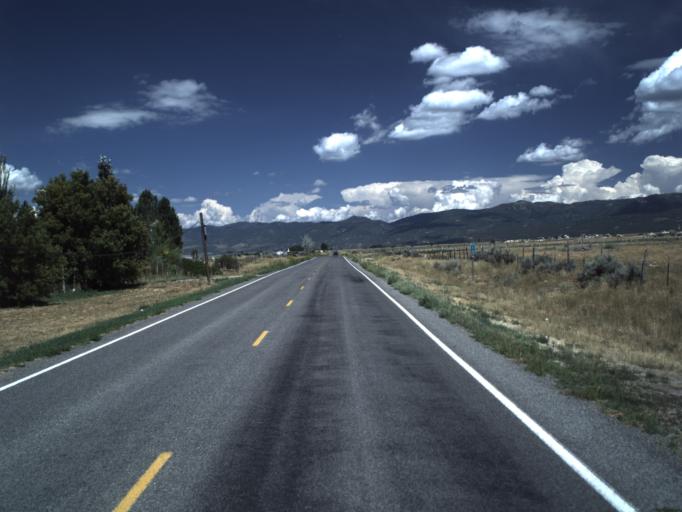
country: US
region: Utah
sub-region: Sanpete County
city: Mount Pleasant
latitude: 39.5014
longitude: -111.4881
